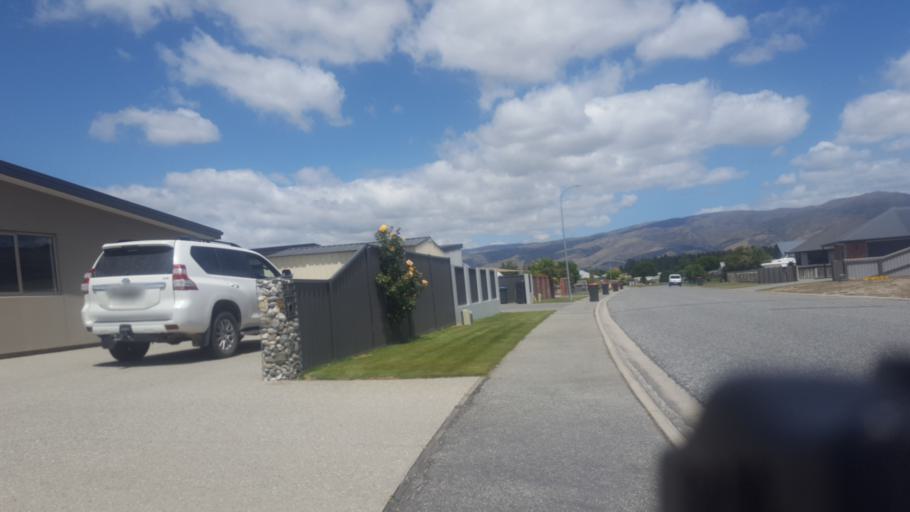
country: NZ
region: Otago
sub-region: Queenstown-Lakes District
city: Wanaka
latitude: -45.0496
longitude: 169.1991
